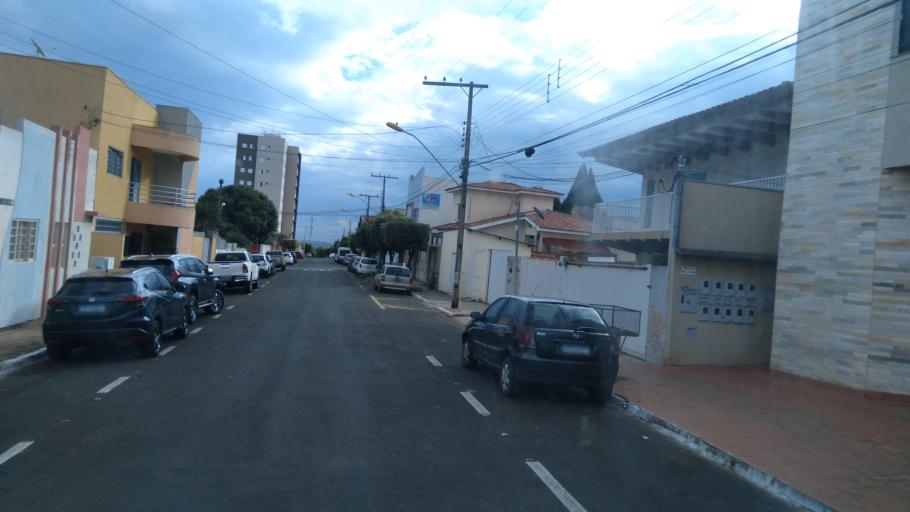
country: BR
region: Goias
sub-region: Mineiros
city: Mineiros
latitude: -17.5673
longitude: -52.5585
